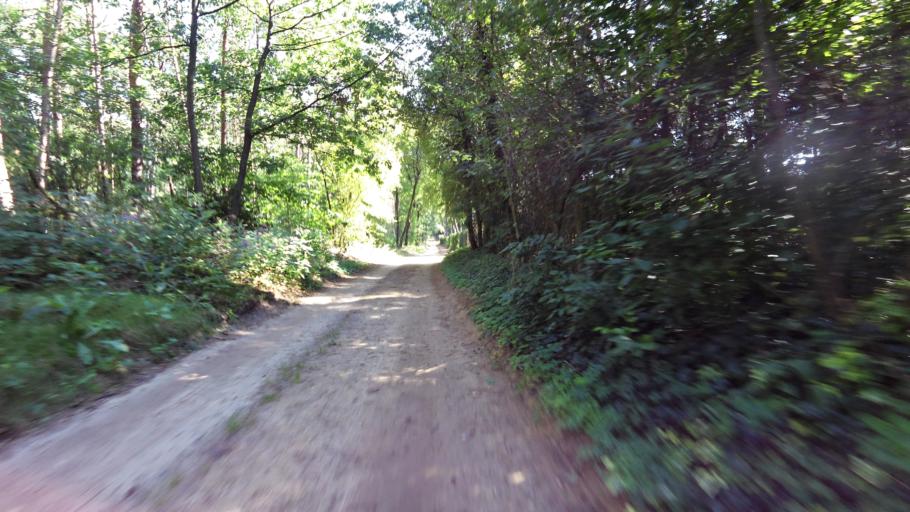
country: NL
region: Gelderland
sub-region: Gemeente Renkum
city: Renkum
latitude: 52.0098
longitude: 5.7243
